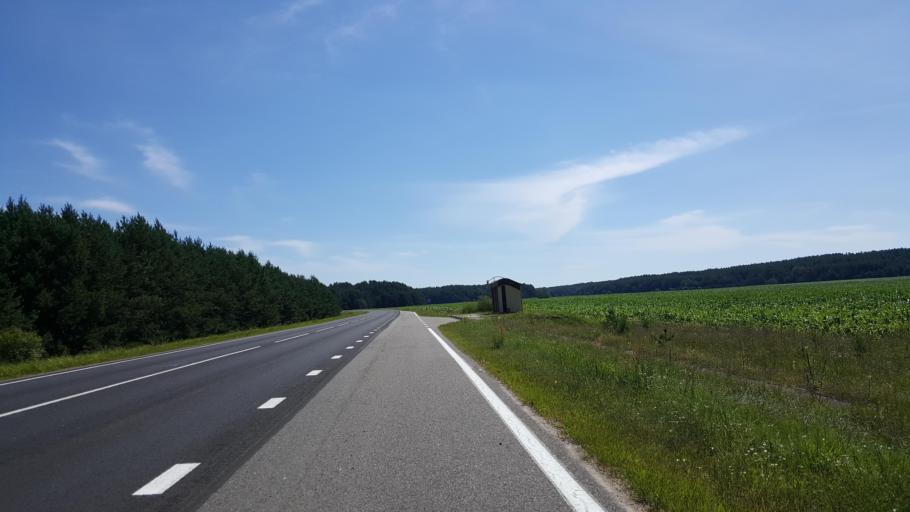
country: BY
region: Brest
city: Zhabinka
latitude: 52.3979
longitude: 24.0376
